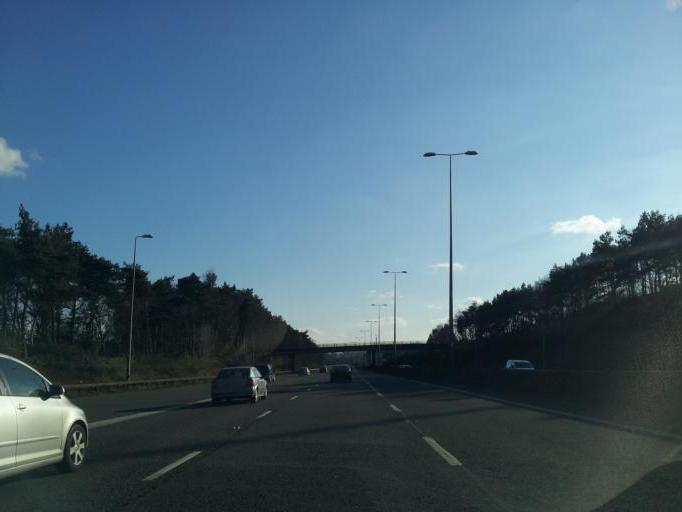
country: GB
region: England
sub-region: Devon
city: Topsham
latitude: 50.7092
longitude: -3.4656
